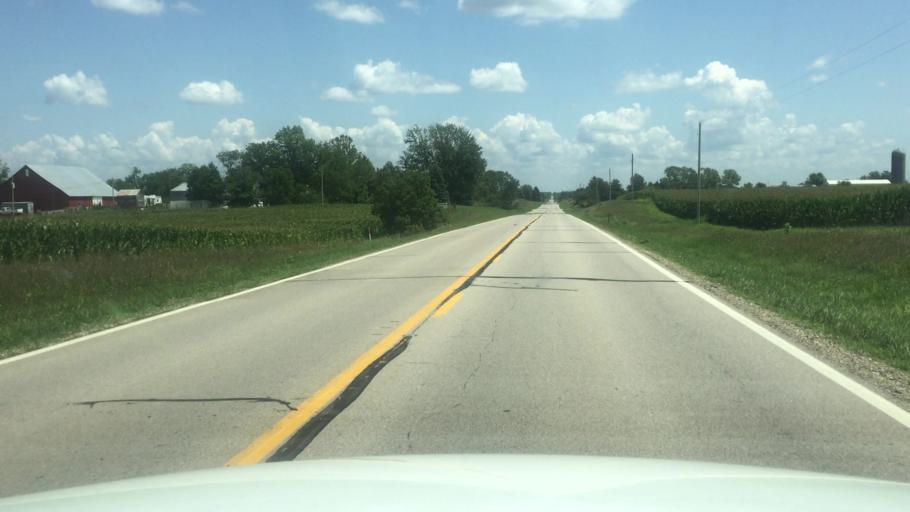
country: US
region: Kansas
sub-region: Brown County
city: Horton
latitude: 39.6674
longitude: -95.5859
